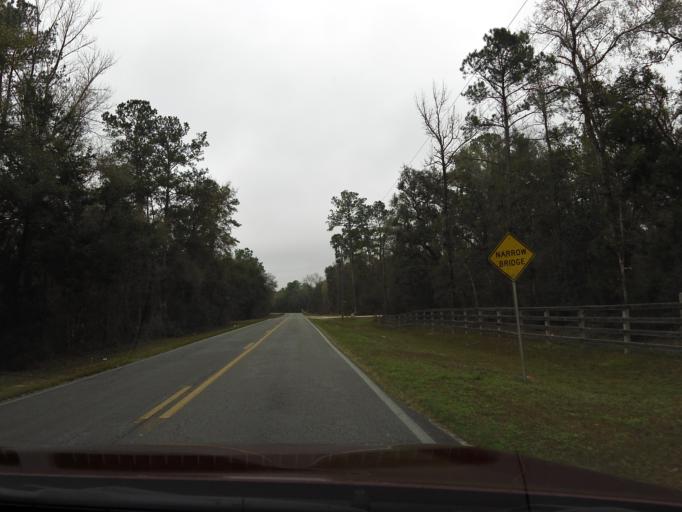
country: US
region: Florida
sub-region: Gilchrist County
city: Trenton
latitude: 29.8007
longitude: -82.9349
